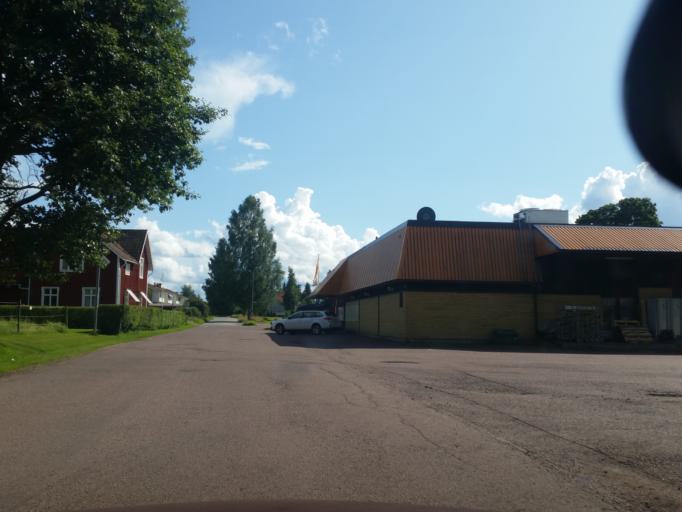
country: SE
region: Dalarna
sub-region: Leksand Municipality
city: Smedby
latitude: 60.6804
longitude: 15.0934
